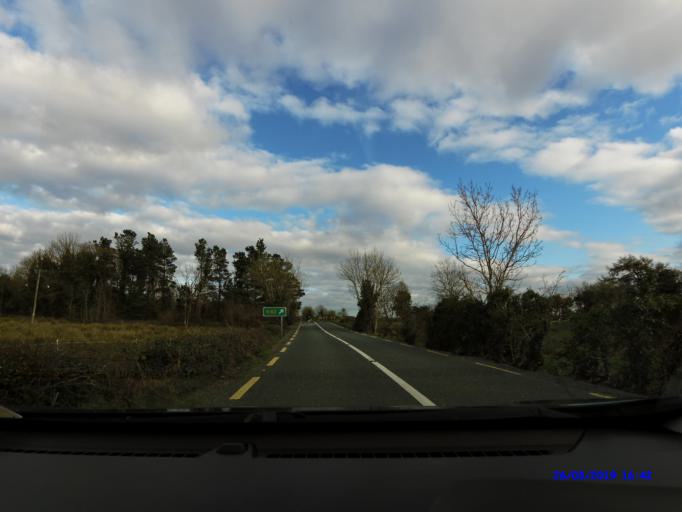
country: IE
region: Connaught
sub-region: Maigh Eo
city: Ballyhaunis
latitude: 53.8662
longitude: -8.7646
